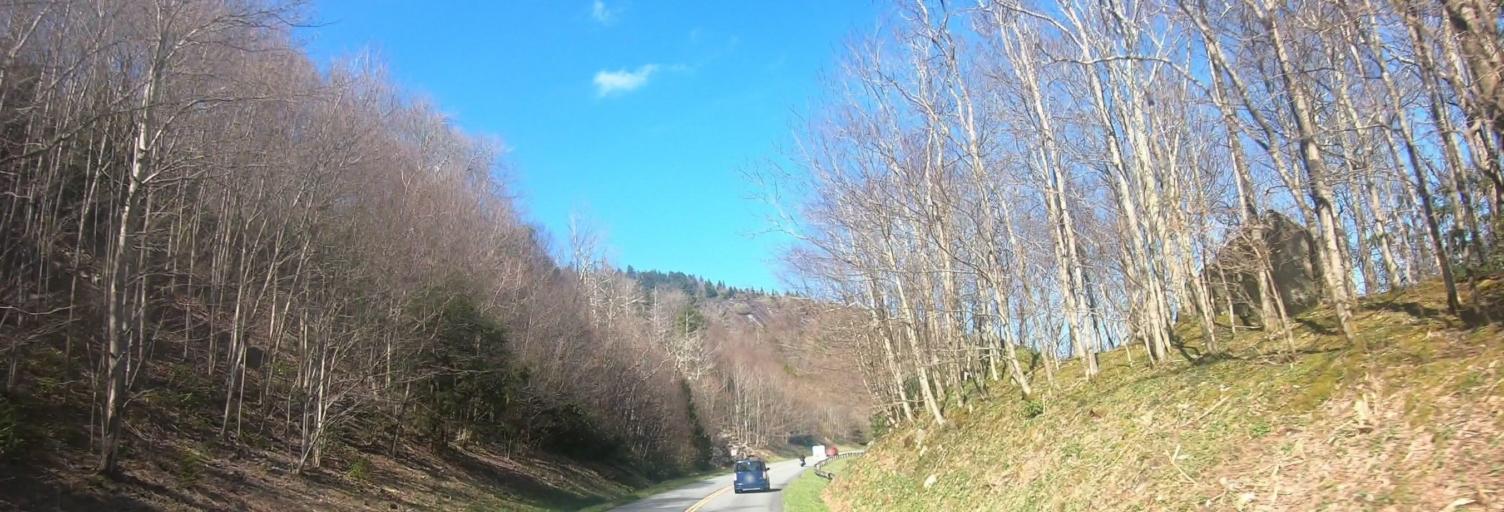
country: US
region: North Carolina
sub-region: Avery County
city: Banner Elk
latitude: 36.0875
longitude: -81.8264
